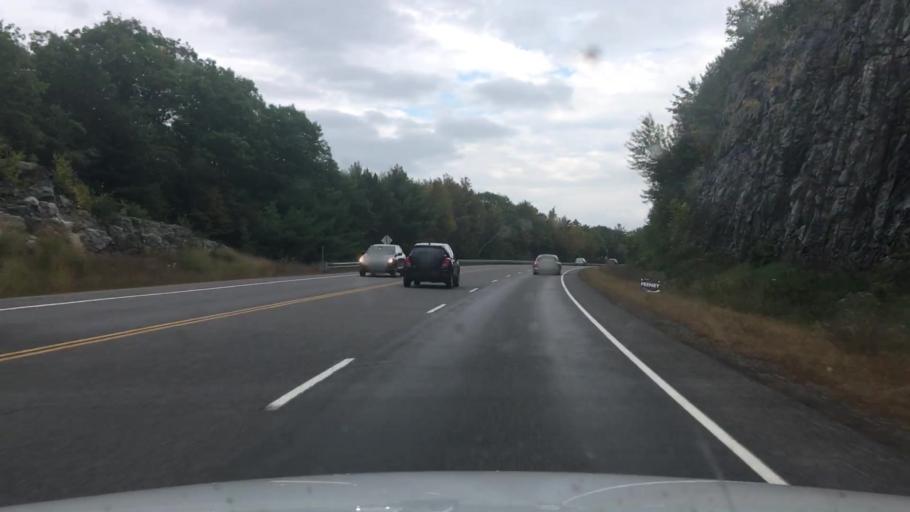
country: US
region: New Hampshire
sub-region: Carroll County
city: Wolfeboro
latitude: 43.5363
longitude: -71.2803
